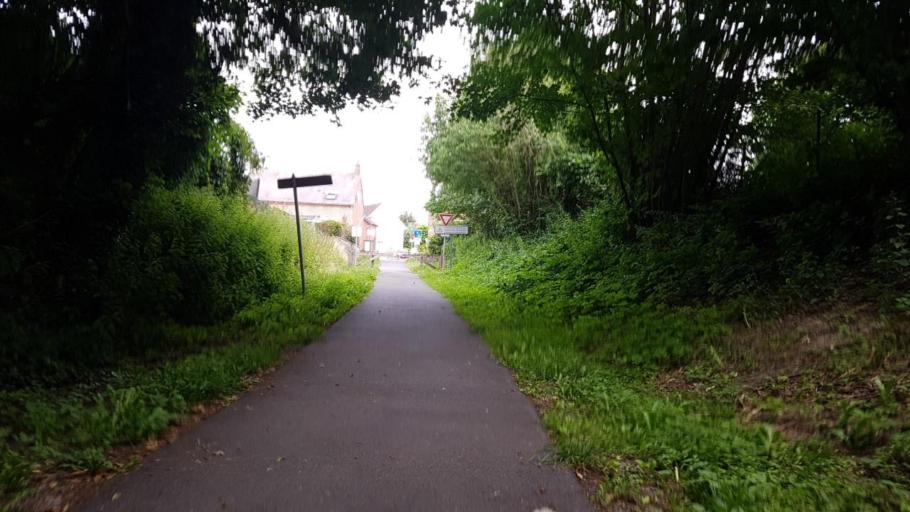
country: FR
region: Picardie
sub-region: Departement de l'Aisne
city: La Capelle
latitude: 49.9059
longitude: 3.9123
